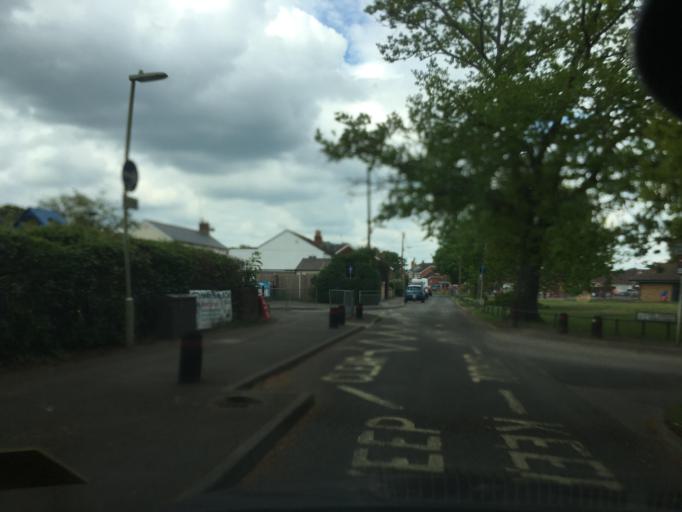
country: GB
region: England
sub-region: Bracknell Forest
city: Sandhurst
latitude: 51.3329
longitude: -0.7956
